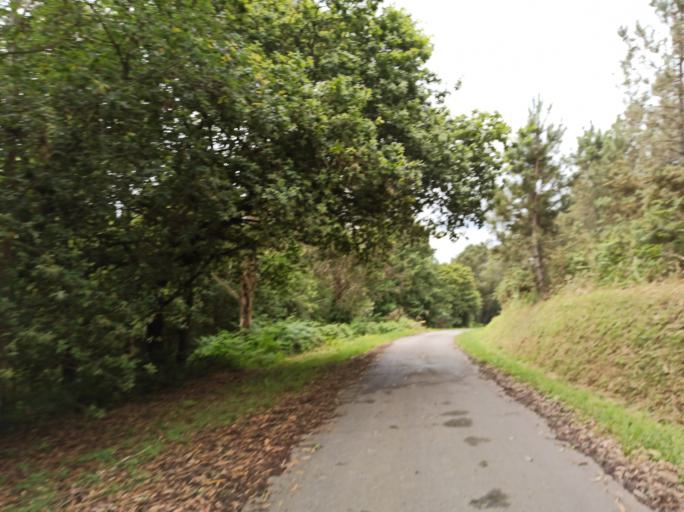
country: ES
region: Galicia
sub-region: Provincia de Pontevedra
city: Silleda
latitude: 42.7687
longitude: -8.1626
